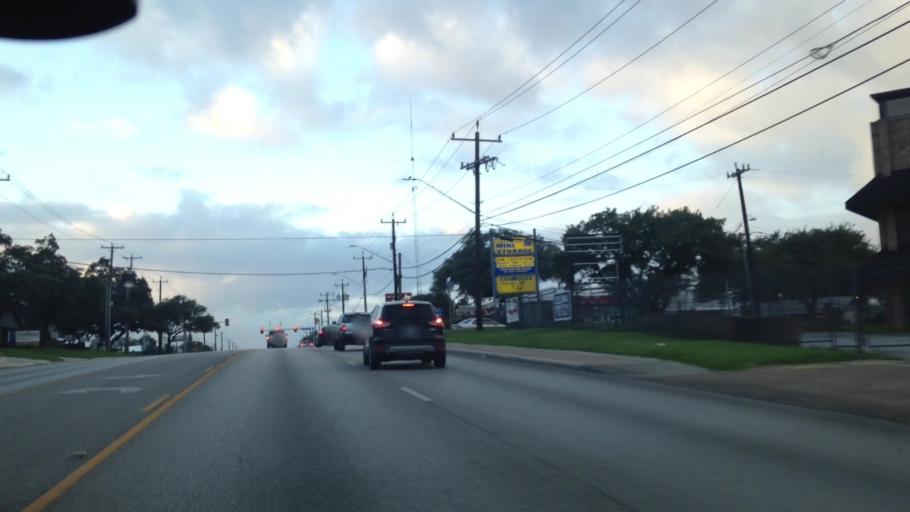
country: US
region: Texas
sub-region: Bexar County
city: Windcrest
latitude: 29.5416
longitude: -98.4111
